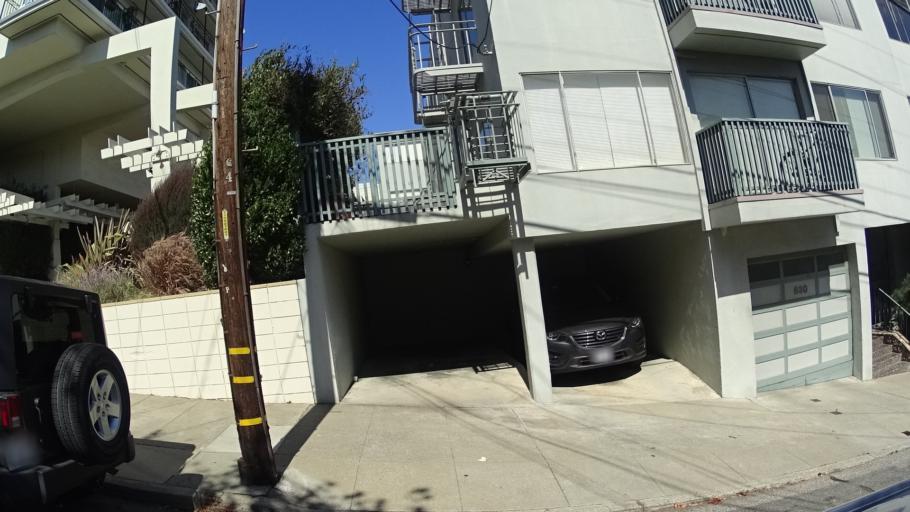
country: US
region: California
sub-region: San Francisco County
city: San Francisco
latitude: 37.7537
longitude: -122.4350
